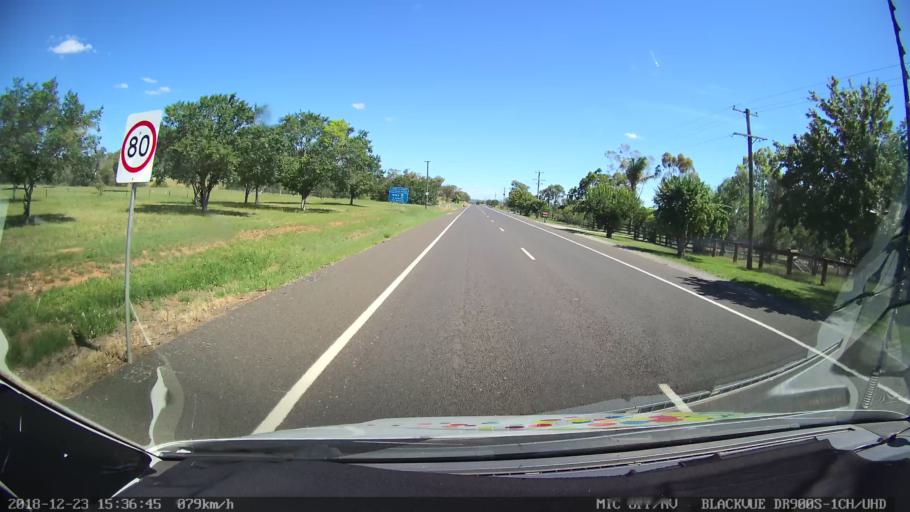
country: AU
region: New South Wales
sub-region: Tamworth Municipality
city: Tamworth
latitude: -31.0445
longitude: 150.8877
